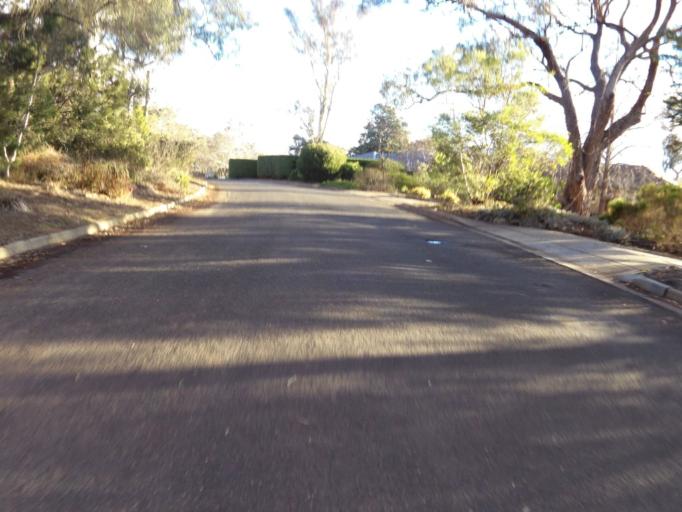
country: AU
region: Australian Capital Territory
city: Canberra
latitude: -35.2711
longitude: 149.1495
